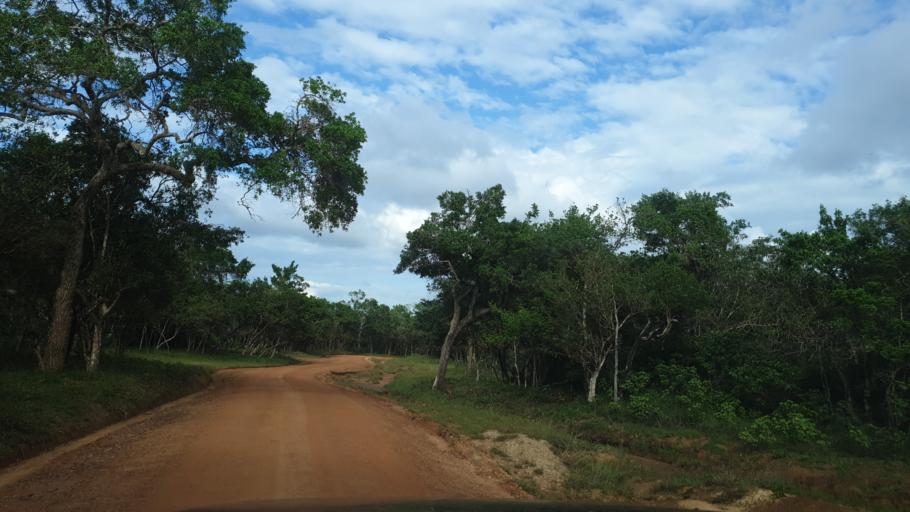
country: LK
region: North Central
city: Anuradhapura
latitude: 8.3626
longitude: 80.0961
